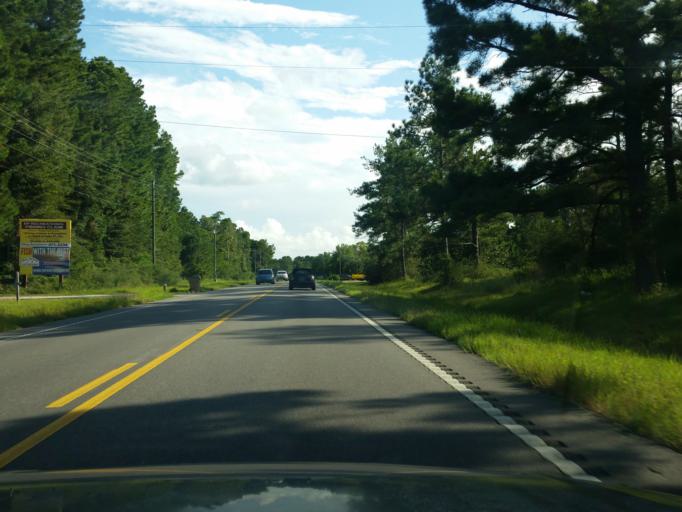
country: US
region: Alabama
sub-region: Mobile County
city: Theodore
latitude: 30.4515
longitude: -88.1161
